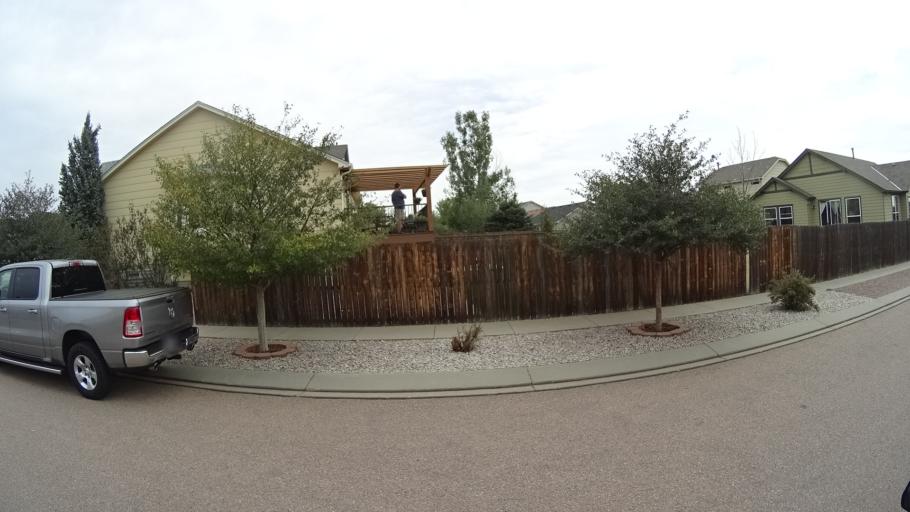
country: US
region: Colorado
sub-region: El Paso County
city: Cimarron Hills
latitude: 38.9161
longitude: -104.6892
